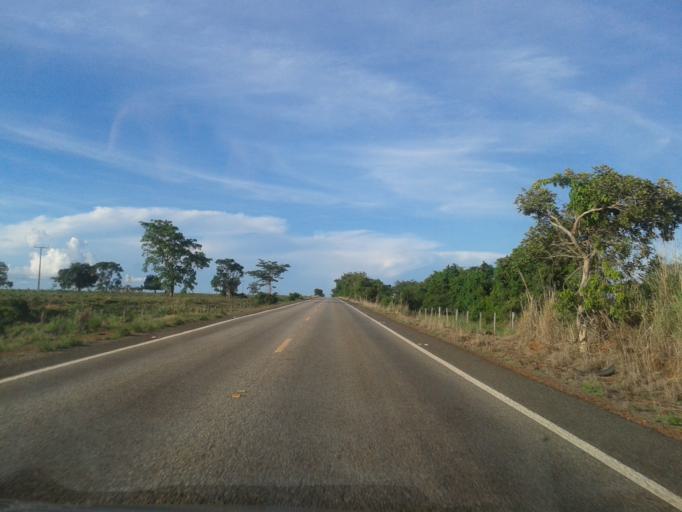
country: BR
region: Goias
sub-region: Sao Miguel Do Araguaia
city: Sao Miguel do Araguaia
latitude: -13.5363
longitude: -50.3062
